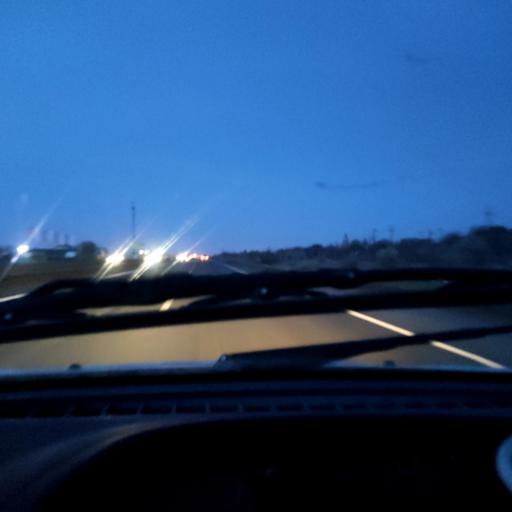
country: RU
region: Samara
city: Tol'yatti
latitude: 53.5698
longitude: 49.3809
